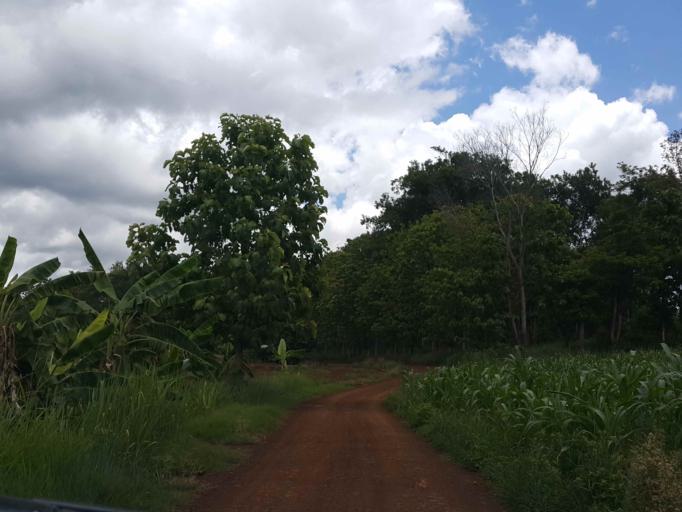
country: TH
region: Chiang Mai
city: Samoeng
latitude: 18.7776
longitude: 98.8266
